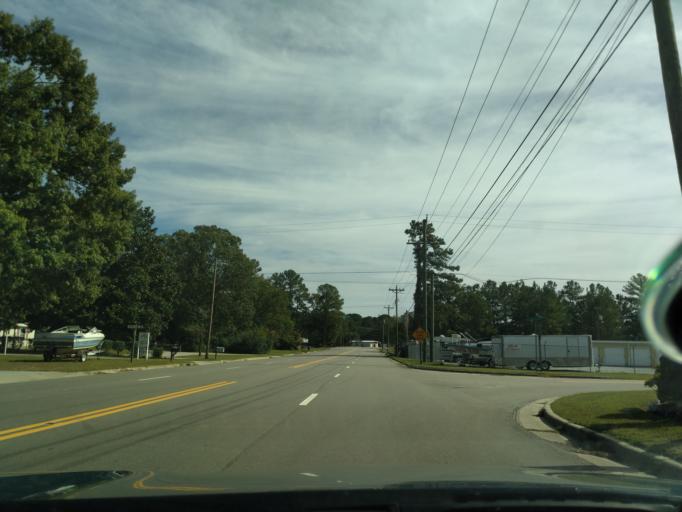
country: US
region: North Carolina
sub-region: Beaufort County
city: River Road
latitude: 35.5212
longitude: -77.0070
